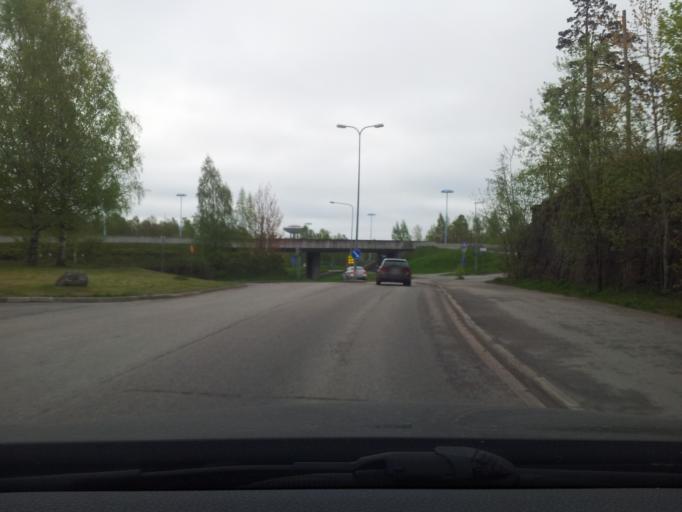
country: FI
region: Uusimaa
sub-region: Helsinki
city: Koukkuniemi
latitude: 60.1682
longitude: 24.7499
